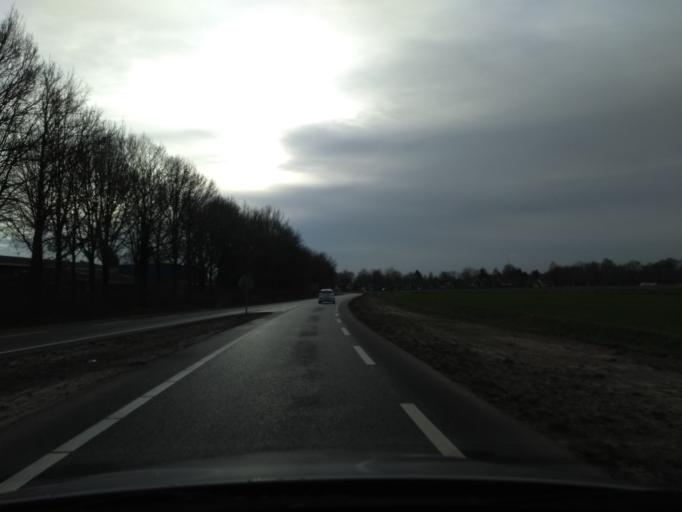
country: NL
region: Overijssel
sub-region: Gemeente Hof van Twente
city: Delden
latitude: 52.2633
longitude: 6.7023
